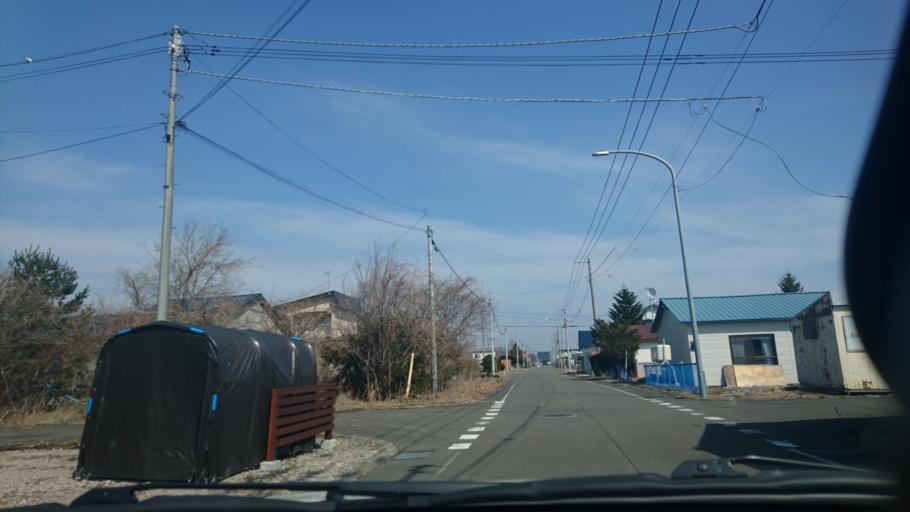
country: JP
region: Hokkaido
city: Otofuke
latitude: 43.0941
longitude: 143.2269
